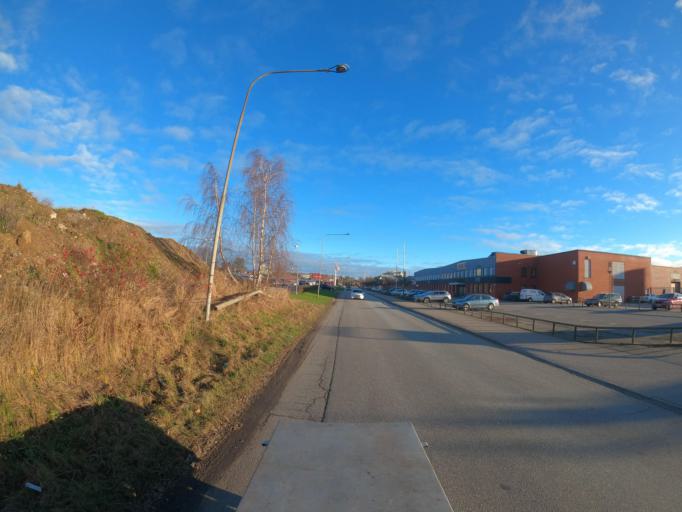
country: SE
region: Skane
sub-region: Svedala Kommun
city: Svedala
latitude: 55.5063
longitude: 13.2301
